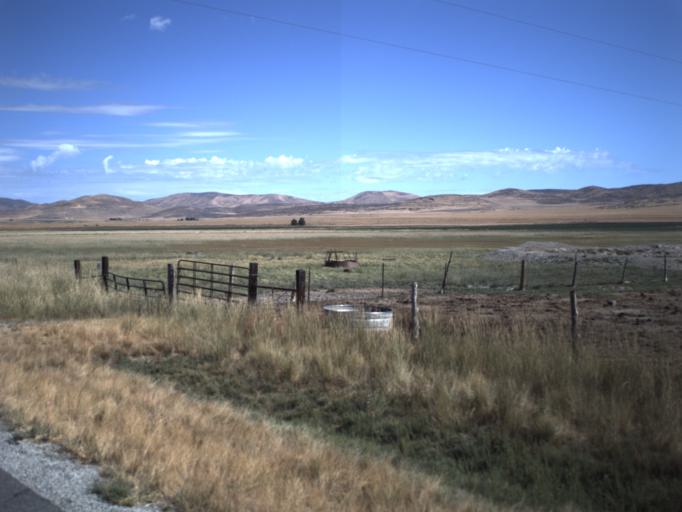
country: US
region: Utah
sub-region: Box Elder County
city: Tremonton
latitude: 41.7580
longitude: -112.4347
